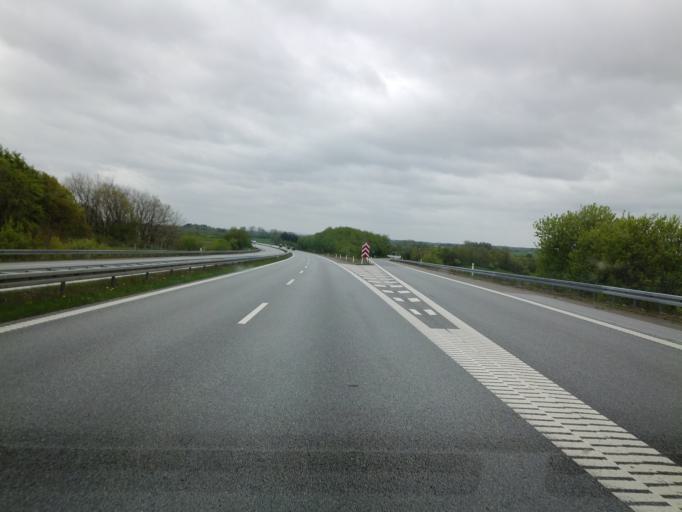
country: DK
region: North Denmark
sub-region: Frederikshavn Kommune
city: Saeby
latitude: 57.3517
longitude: 10.4624
